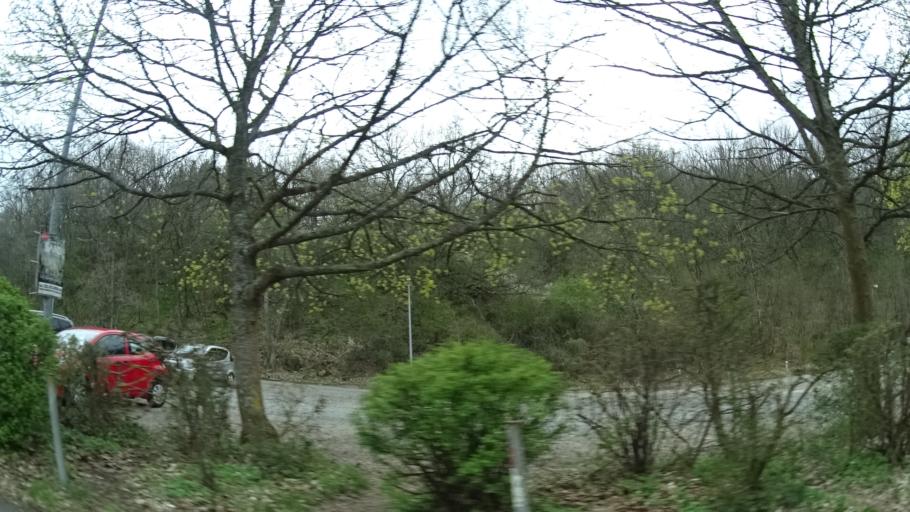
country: DE
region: Rheinland-Pfalz
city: Idar-Oberstein
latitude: 49.7167
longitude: 7.3237
